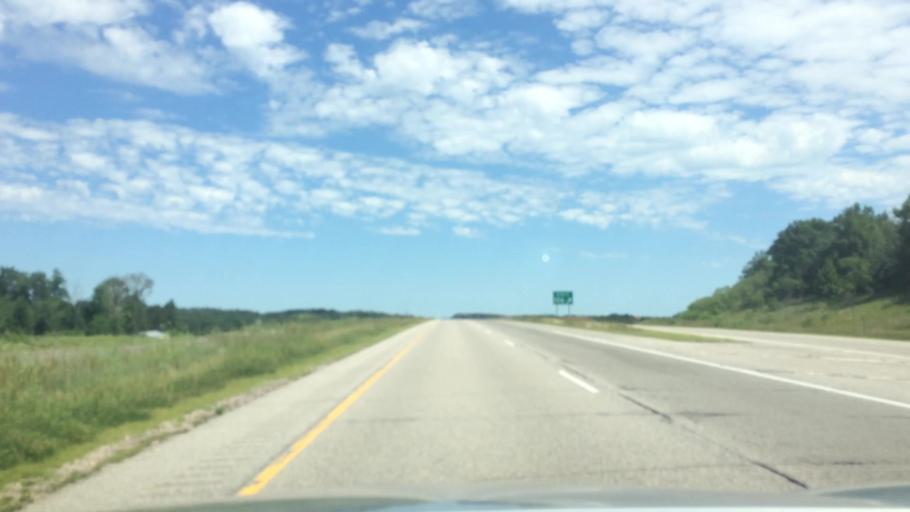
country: US
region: Wisconsin
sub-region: Marquette County
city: Westfield
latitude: 43.7861
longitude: -89.4835
